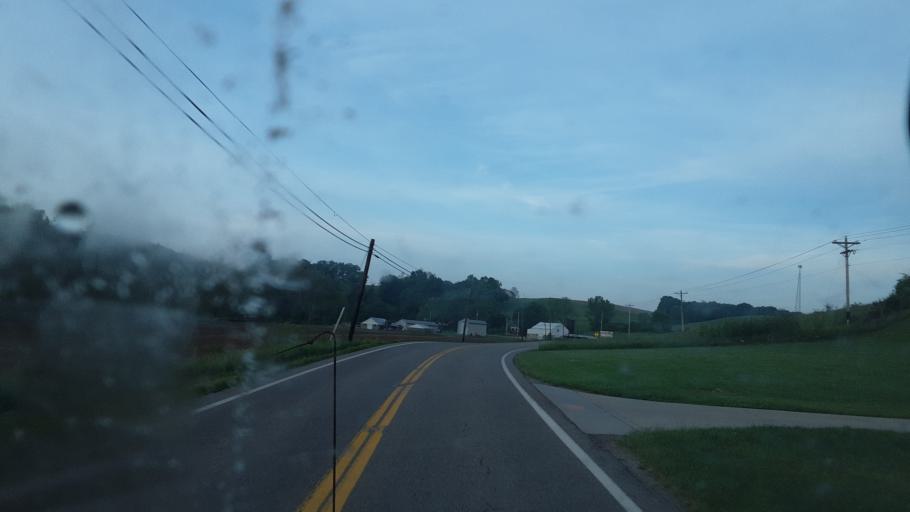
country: US
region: Ohio
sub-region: Ross County
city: Kingston
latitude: 39.4897
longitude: -82.7329
